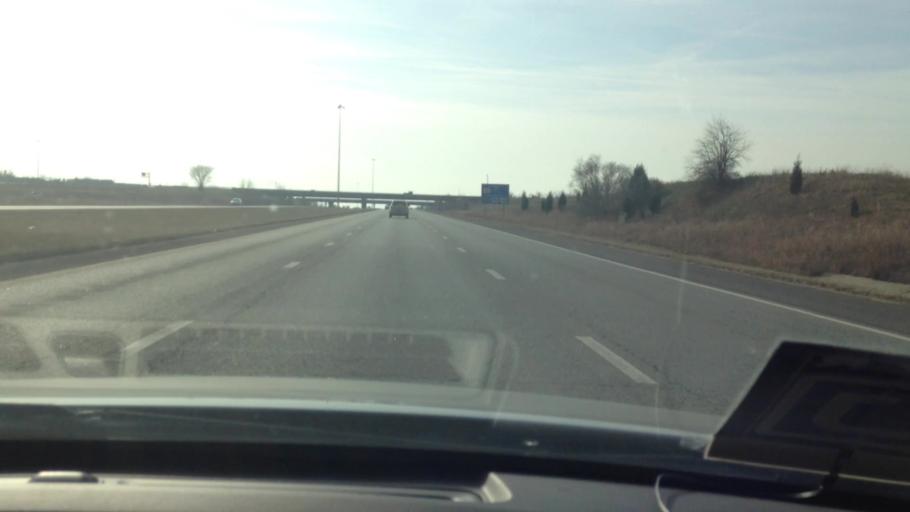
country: US
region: Kansas
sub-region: Wyandotte County
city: Edwardsville
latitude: 39.0158
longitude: -94.7825
